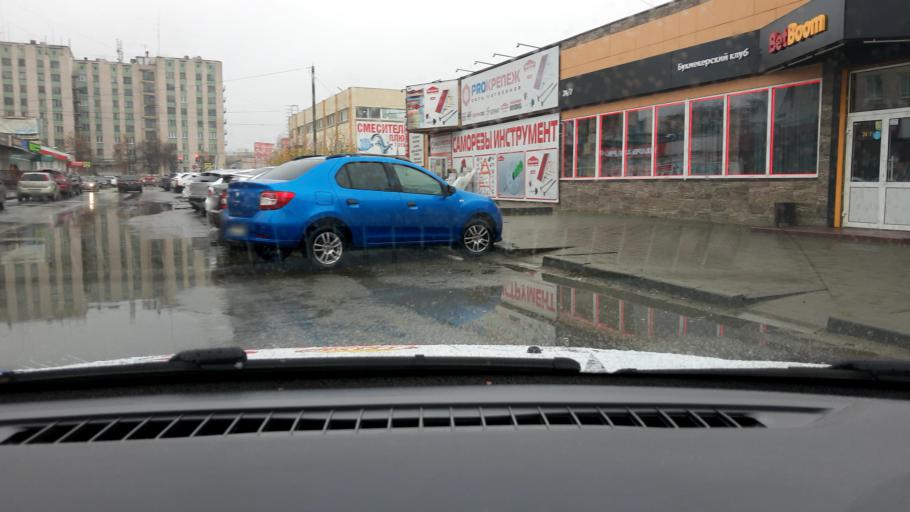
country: RU
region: Nizjnij Novgorod
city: Dzerzhinsk
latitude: 56.2341
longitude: 43.4350
